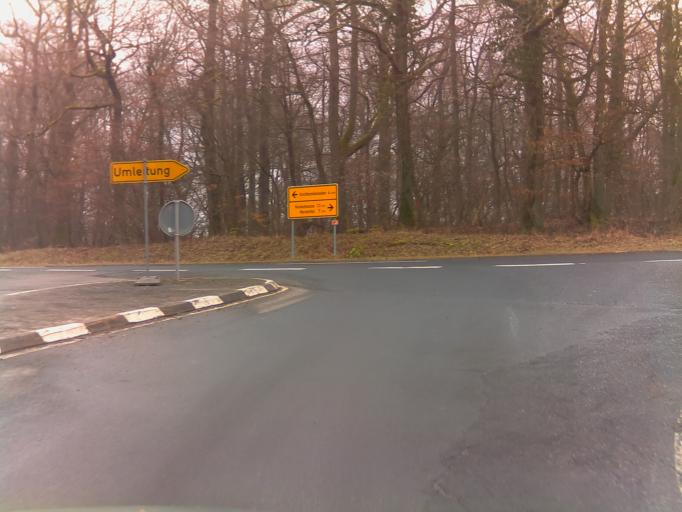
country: DE
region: Rheinland-Pfalz
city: Dannenfels
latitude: 49.6605
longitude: 7.9569
